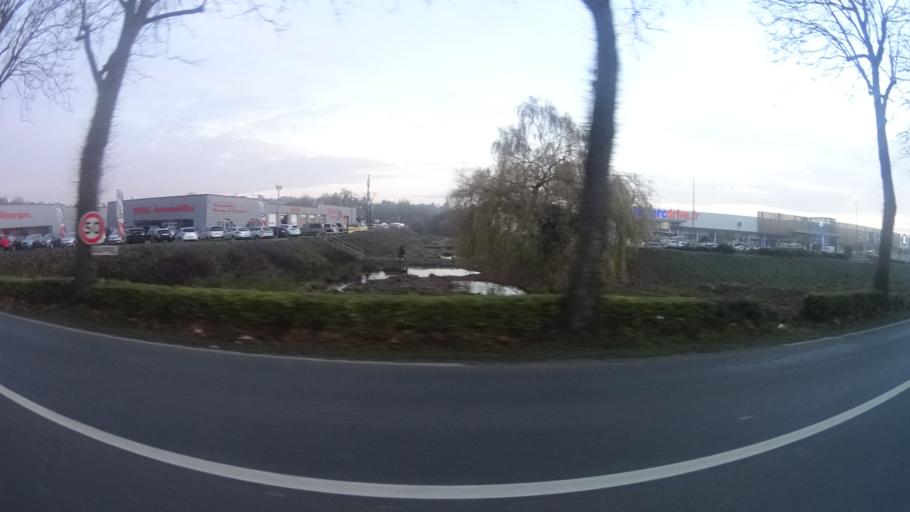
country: FR
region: Brittany
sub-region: Departement d'Ille-et-Vilaine
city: Redon
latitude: 47.6469
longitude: -2.0797
